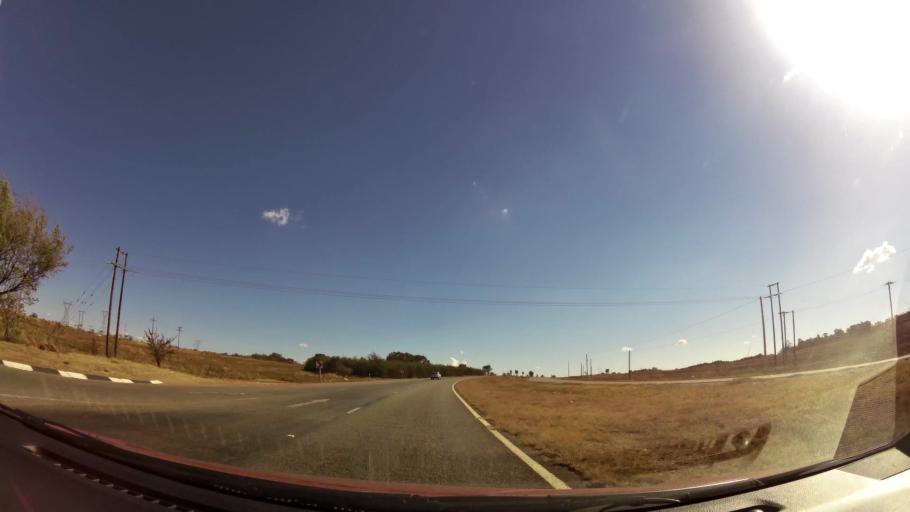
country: ZA
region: Gauteng
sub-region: West Rand District Municipality
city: Carletonville
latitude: -26.4177
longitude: 27.4425
